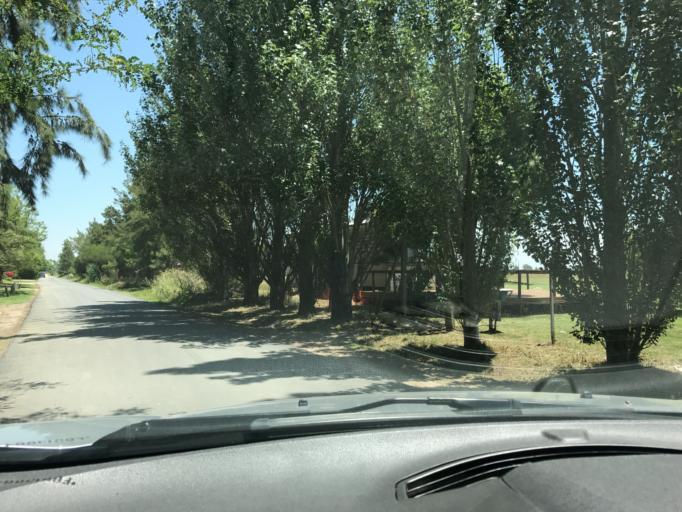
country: AR
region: Buenos Aires
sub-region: Partido de La Plata
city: La Plata
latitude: -34.8599
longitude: -58.0471
